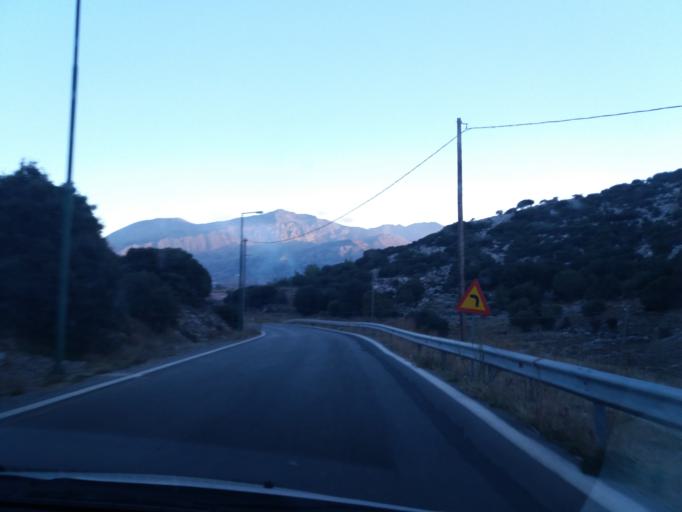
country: GR
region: Crete
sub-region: Nomos Irakleiou
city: Mokhos
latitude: 35.2007
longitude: 25.4599
